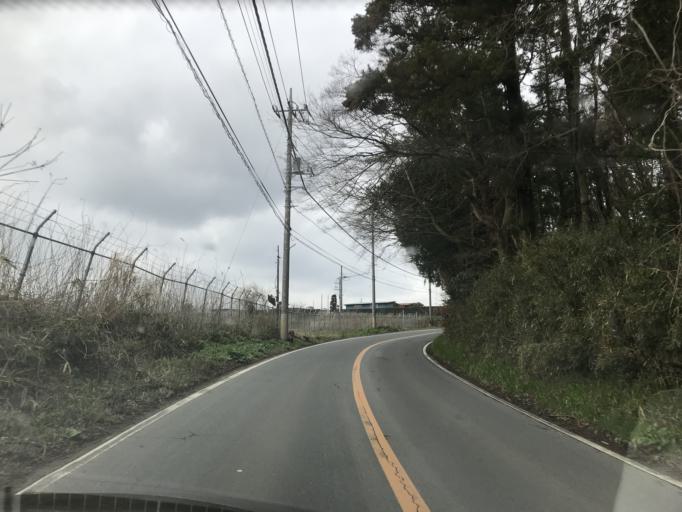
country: JP
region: Chiba
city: Sawara
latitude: 35.8405
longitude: 140.5057
